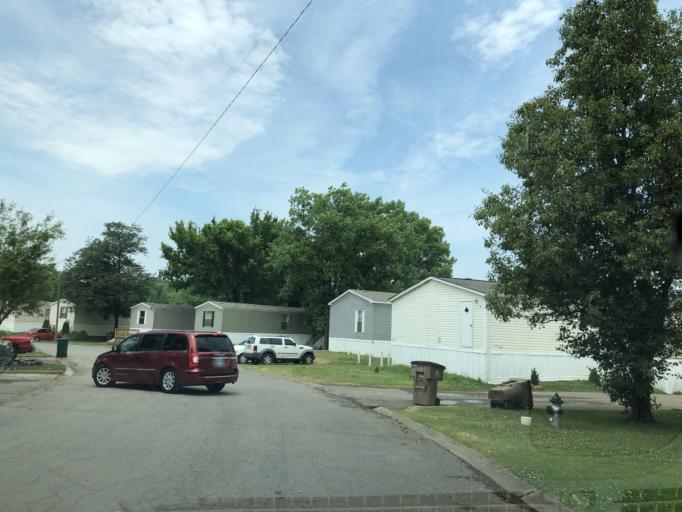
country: US
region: Tennessee
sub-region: Davidson County
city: Oak Hill
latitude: 36.0751
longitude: -86.6769
